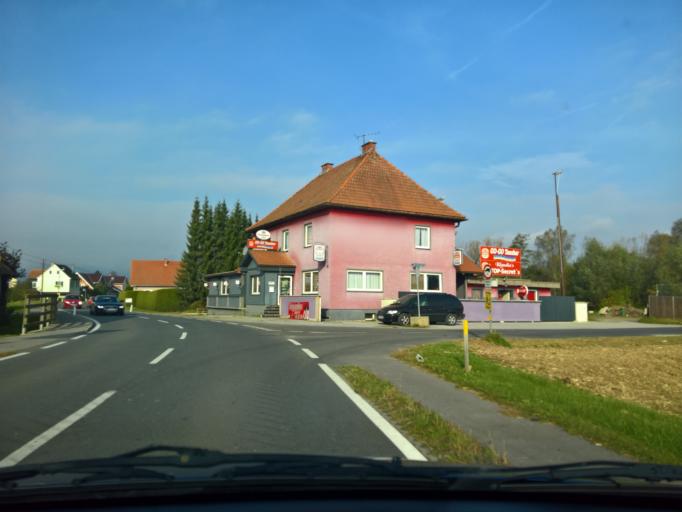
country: AT
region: Styria
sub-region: Politischer Bezirk Deutschlandsberg
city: Rassach
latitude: 46.8237
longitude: 15.2778
